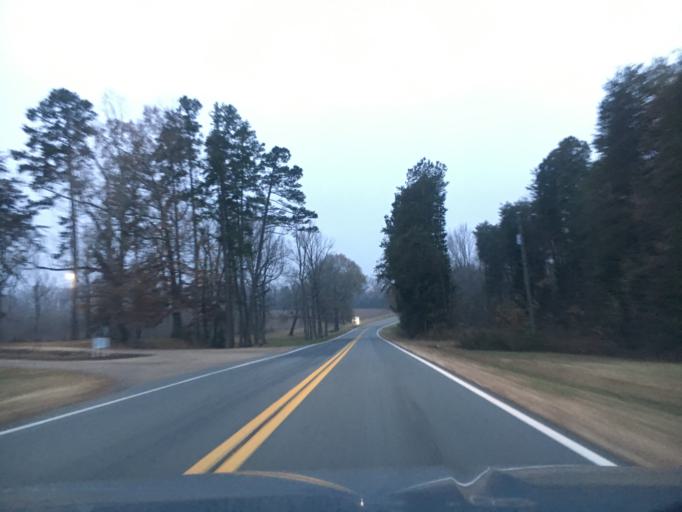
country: US
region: Virginia
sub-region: Halifax County
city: South Boston
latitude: 36.7067
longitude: -78.9474
